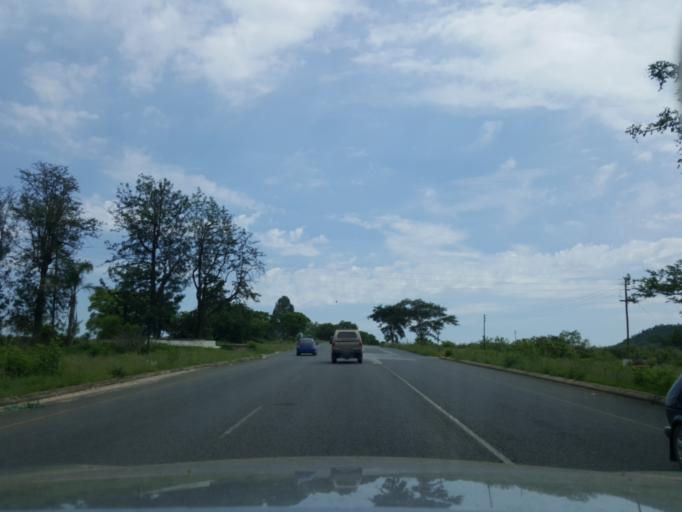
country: ZA
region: Mpumalanga
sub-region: Ehlanzeni District
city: Nelspruit
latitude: -25.4505
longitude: 31.0962
